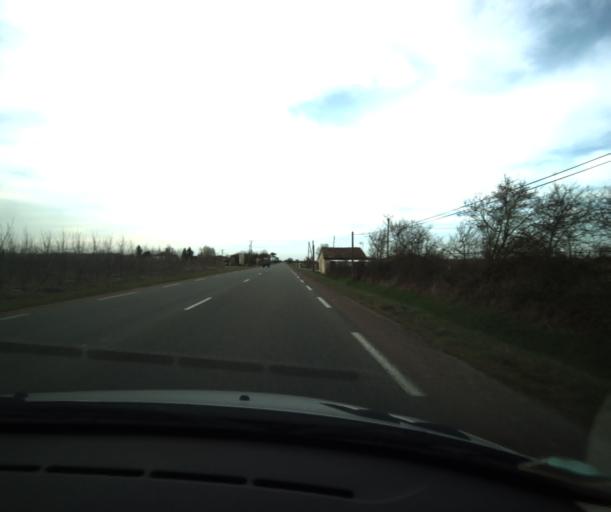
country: FR
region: Midi-Pyrenees
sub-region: Departement du Tarn-et-Garonne
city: Montech
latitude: 43.9641
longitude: 1.2096
